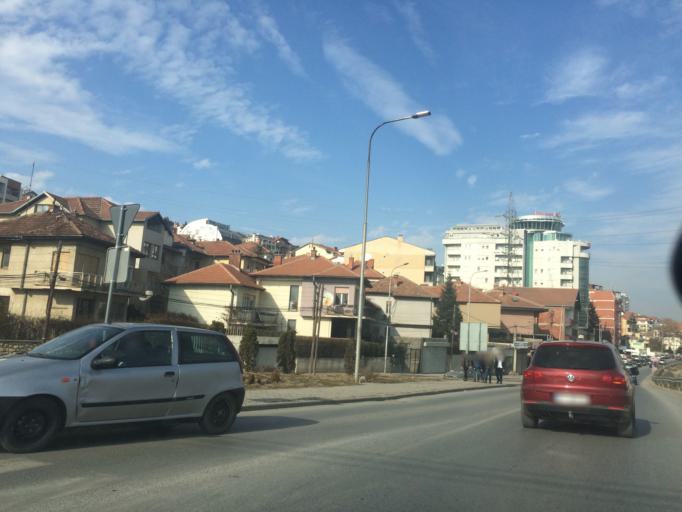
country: XK
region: Pristina
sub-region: Komuna e Prishtines
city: Pristina
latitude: 42.6639
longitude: 21.1549
